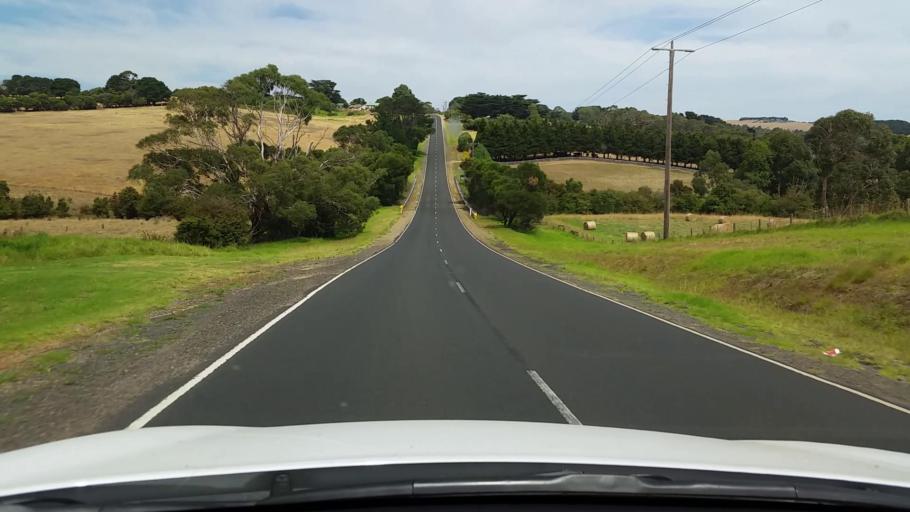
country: AU
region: Victoria
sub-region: Mornington Peninsula
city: Merricks
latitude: -38.4493
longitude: 145.0292
